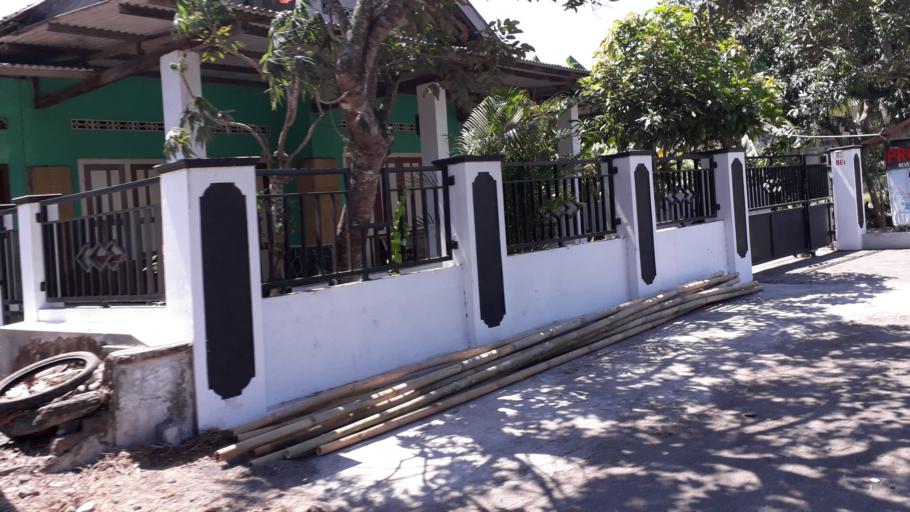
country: ID
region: Daerah Istimewa Yogyakarta
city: Pundong
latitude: -7.9806
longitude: 110.3168
